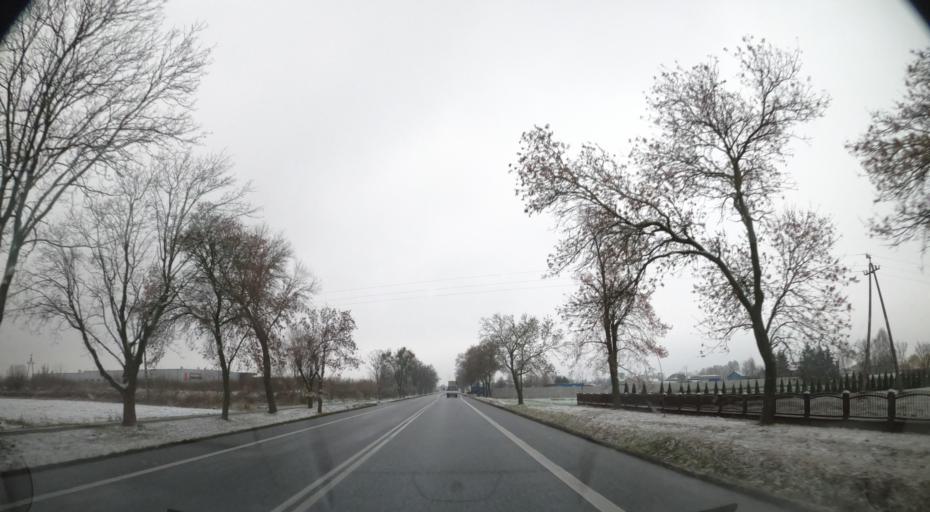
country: PL
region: Masovian Voivodeship
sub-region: Powiat warszawski zachodni
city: Bieniewice
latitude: 52.2034
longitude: 20.5227
